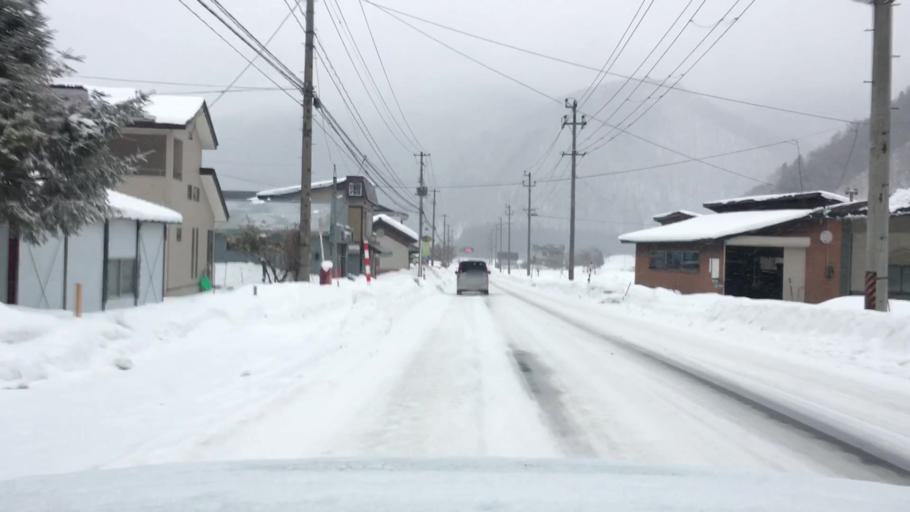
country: JP
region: Akita
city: Hanawa
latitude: 40.0761
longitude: 141.0211
